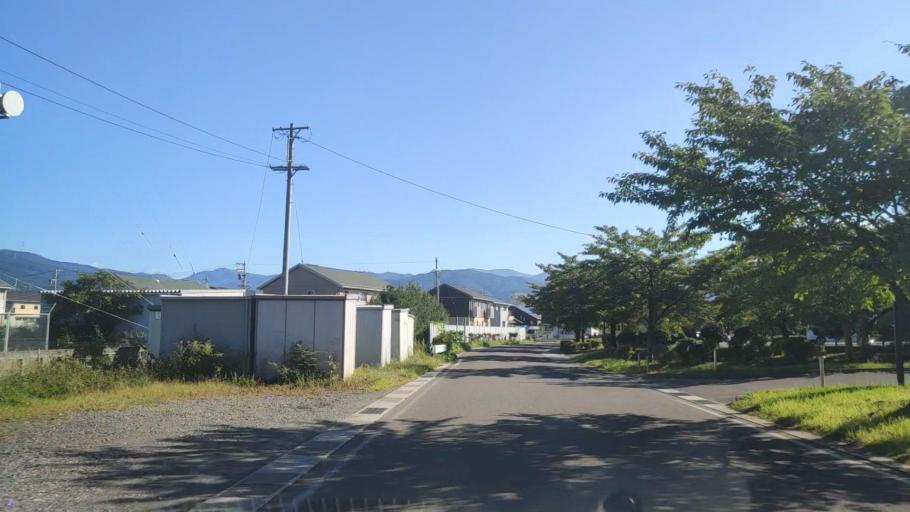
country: JP
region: Nagano
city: Okaya
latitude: 36.0582
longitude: 138.0625
